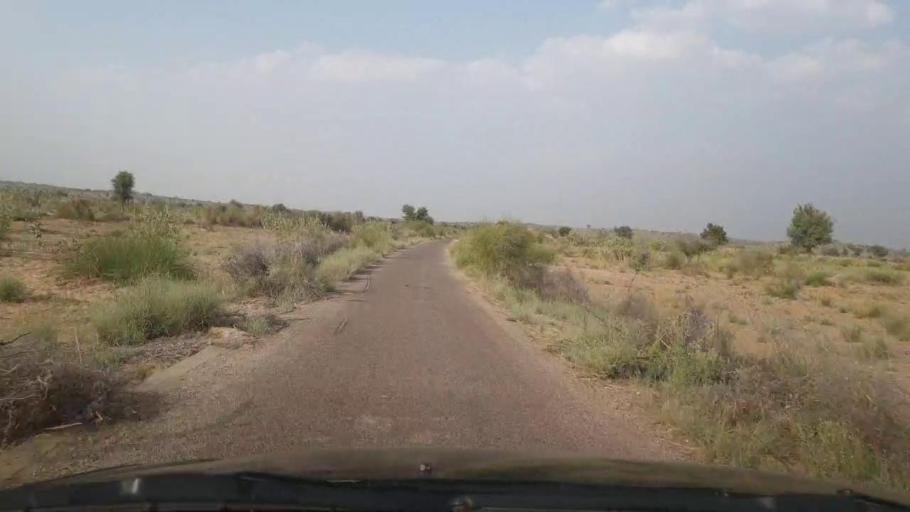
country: PK
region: Sindh
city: Islamkot
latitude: 25.0607
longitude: 70.5616
